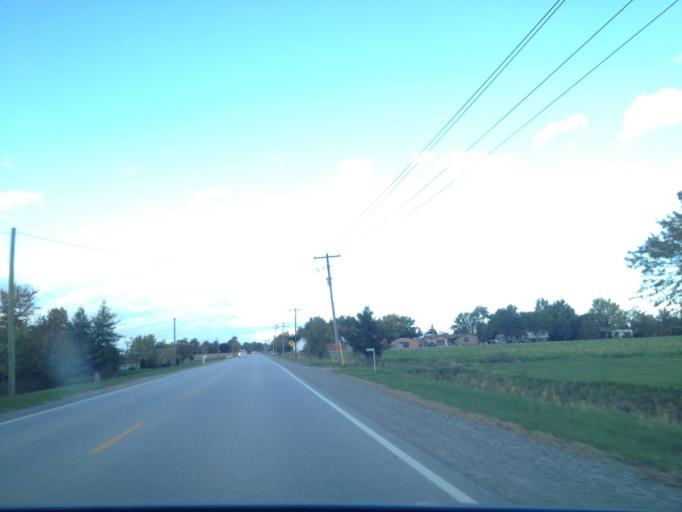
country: US
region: Michigan
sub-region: Wayne County
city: Grosse Pointe
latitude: 42.1619
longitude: -82.7317
